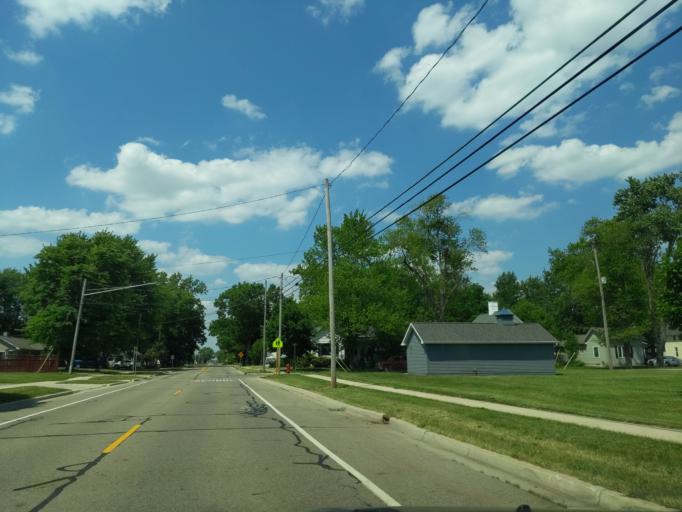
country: US
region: Michigan
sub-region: Clinton County
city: Saint Johns
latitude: 43.0104
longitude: -84.5626
